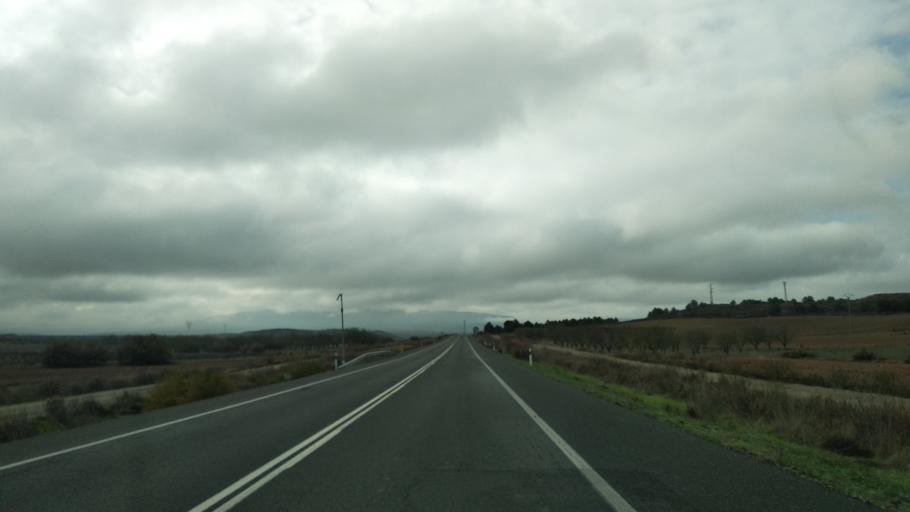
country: ES
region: La Rioja
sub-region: Provincia de La Rioja
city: Pradejon
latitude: 42.3209
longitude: -2.0287
